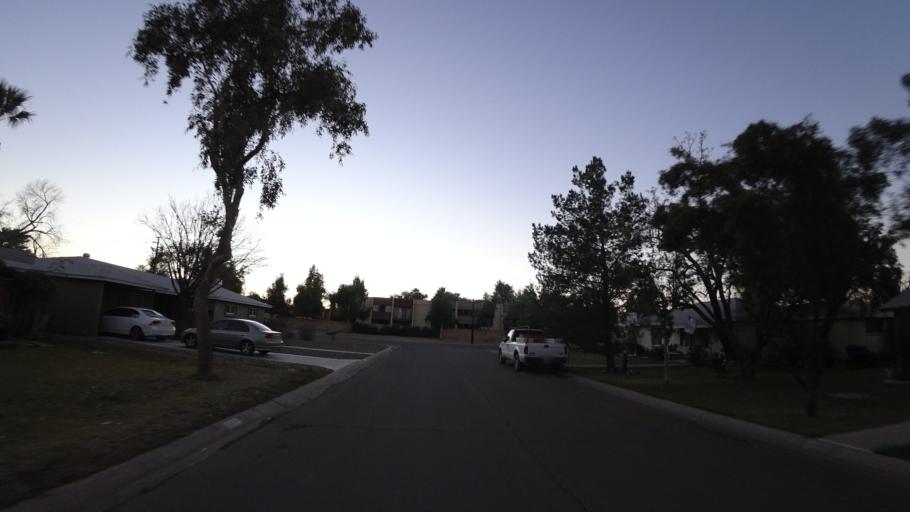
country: US
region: Arizona
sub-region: Maricopa County
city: Tempe Junction
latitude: 33.4139
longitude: -111.9474
